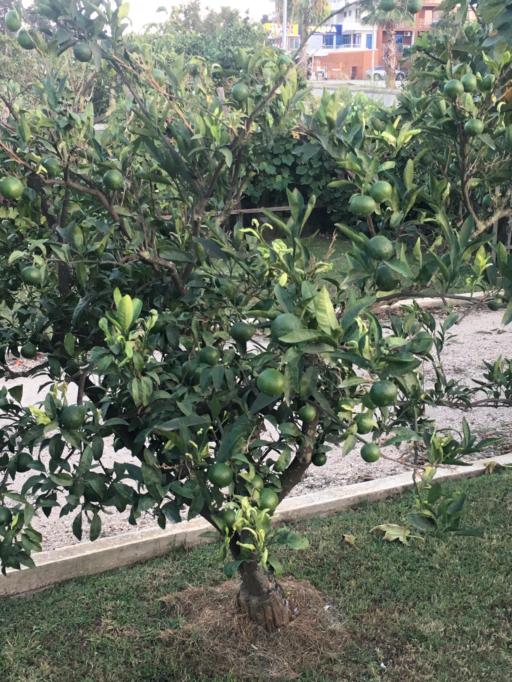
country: ME
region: Ulcinj
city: Ulcinj
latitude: 41.9202
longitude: 19.2382
